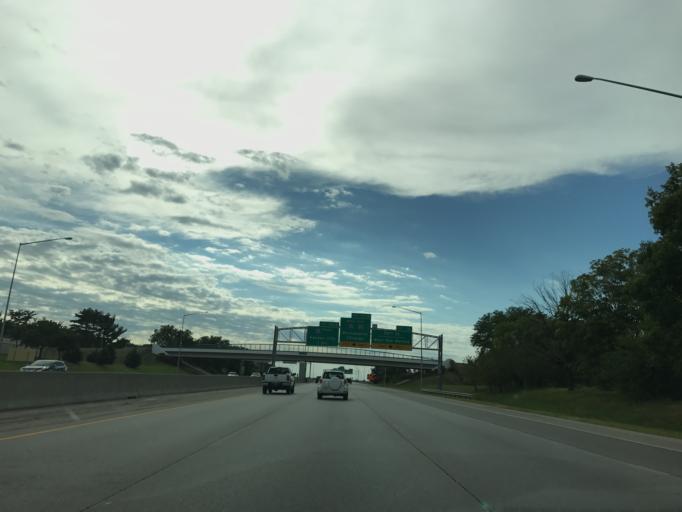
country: US
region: Iowa
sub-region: Polk County
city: Clive
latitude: 41.5924
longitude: -93.7592
